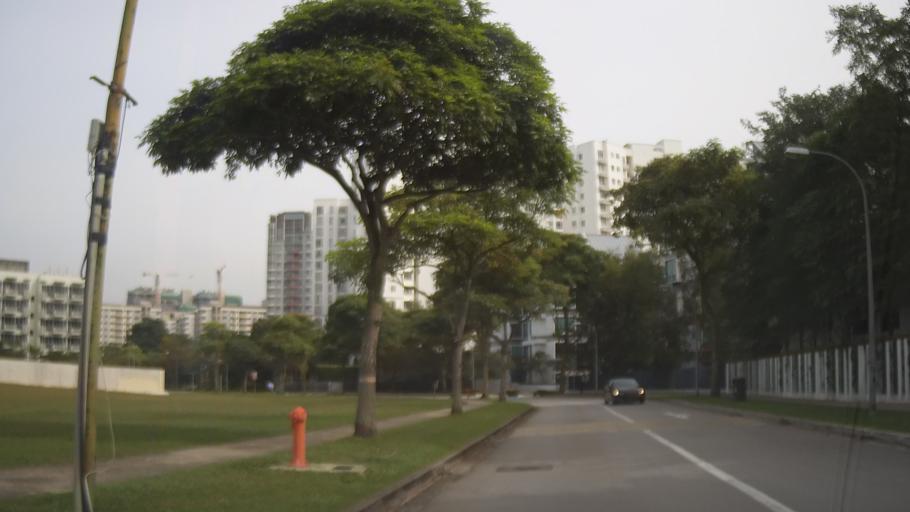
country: MY
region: Johor
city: Johor Bahru
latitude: 1.4285
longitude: 103.7852
